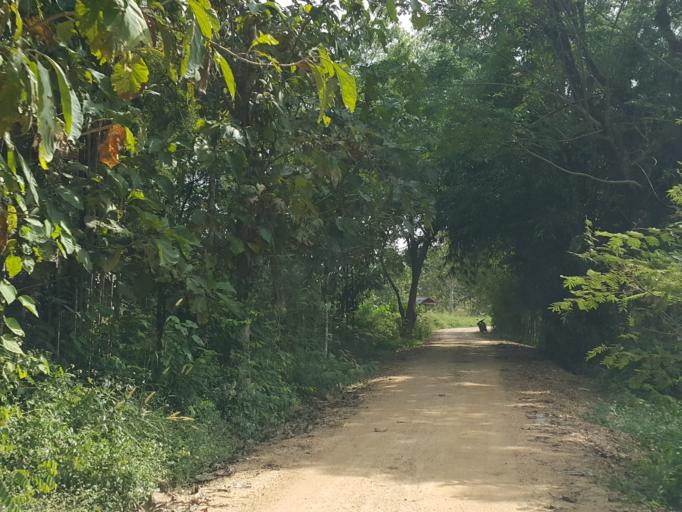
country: TH
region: Lampang
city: Hang Chat
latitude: 18.4870
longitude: 99.4008
